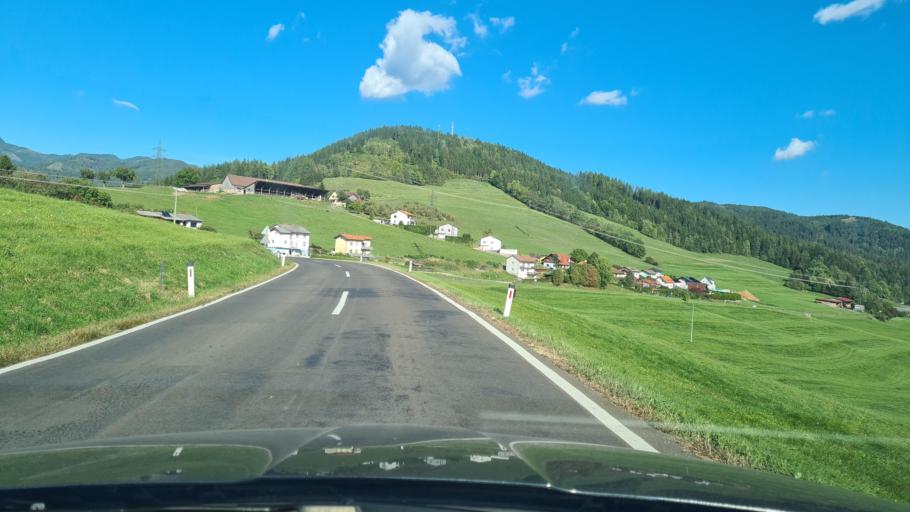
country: AT
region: Styria
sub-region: Politischer Bezirk Leoben
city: Trofaiach
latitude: 47.4031
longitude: 15.0051
